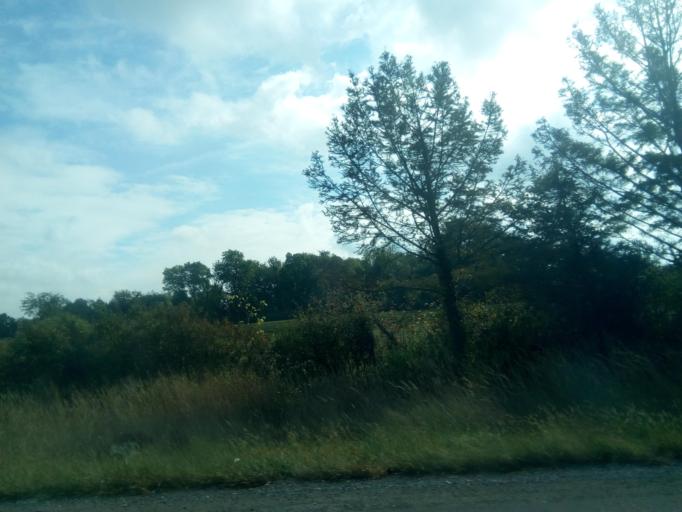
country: US
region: Illinois
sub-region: Saint Clair County
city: Alorton
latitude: 38.5974
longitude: -90.0882
